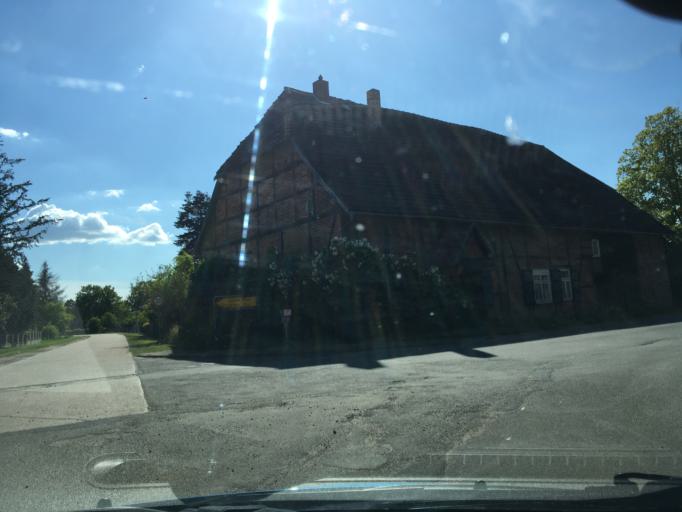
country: DE
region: Brandenburg
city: Lanz
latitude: 53.0380
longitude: 11.5643
